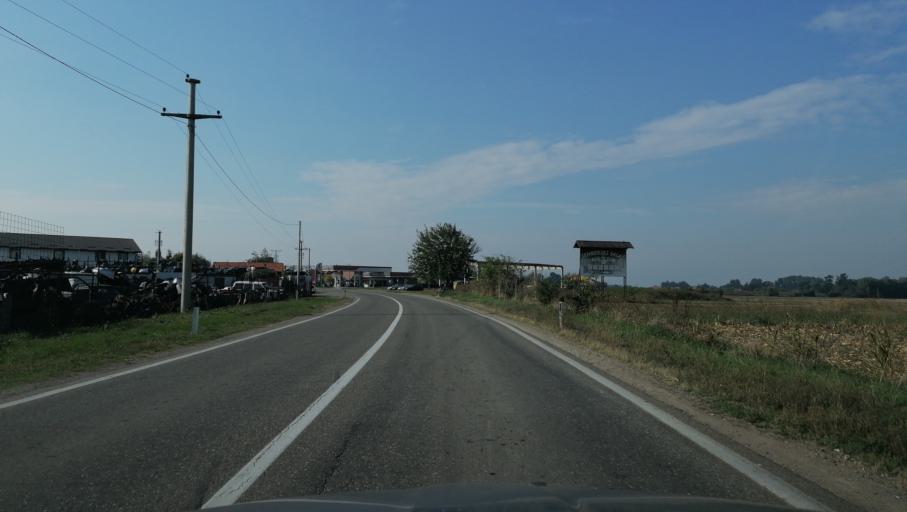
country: BA
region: Republika Srpska
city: Popovi
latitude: 44.7848
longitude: 19.2816
